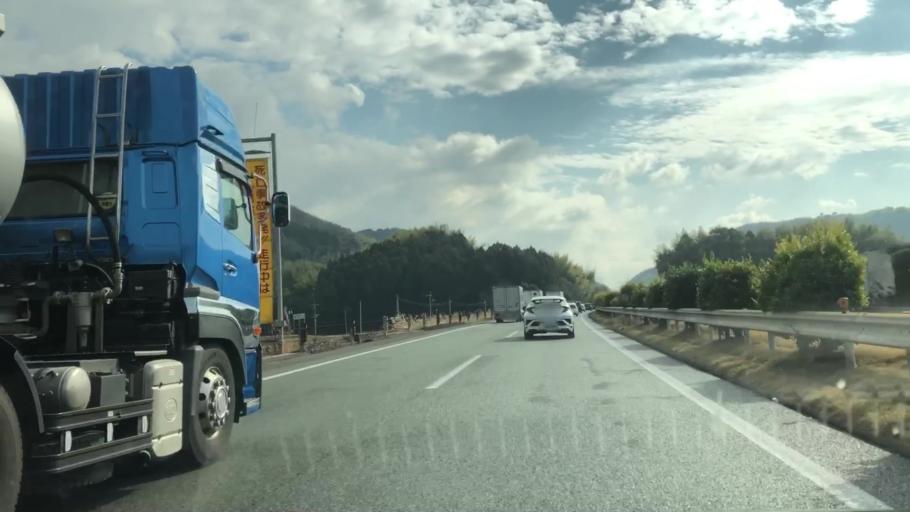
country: JP
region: Fukuoka
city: Setakamachi-takayanagi
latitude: 33.1075
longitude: 130.5336
